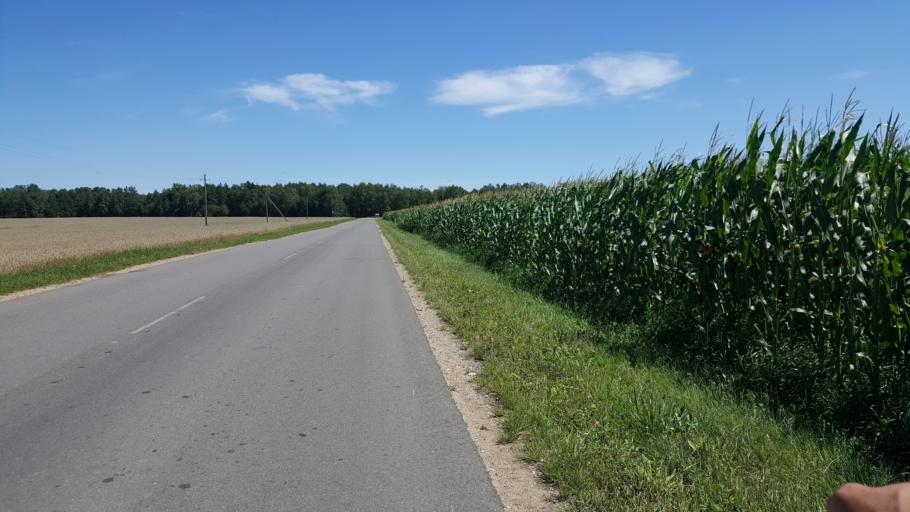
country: BY
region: Brest
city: Charnawchytsy
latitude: 52.2271
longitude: 23.7993
